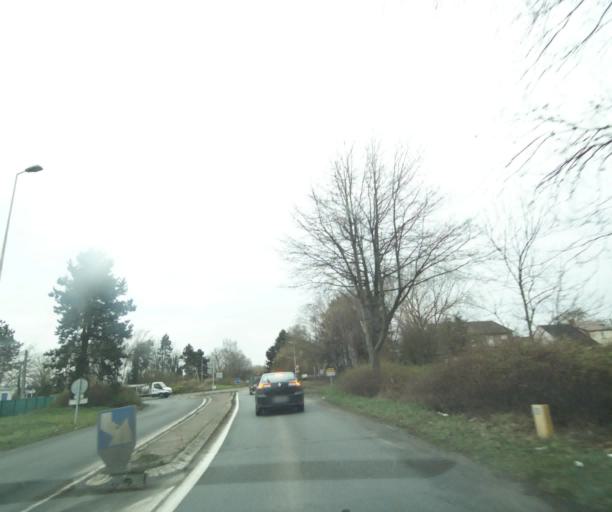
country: FR
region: Nord-Pas-de-Calais
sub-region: Departement du Nord
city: Vicq
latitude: 50.4062
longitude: 3.6068
